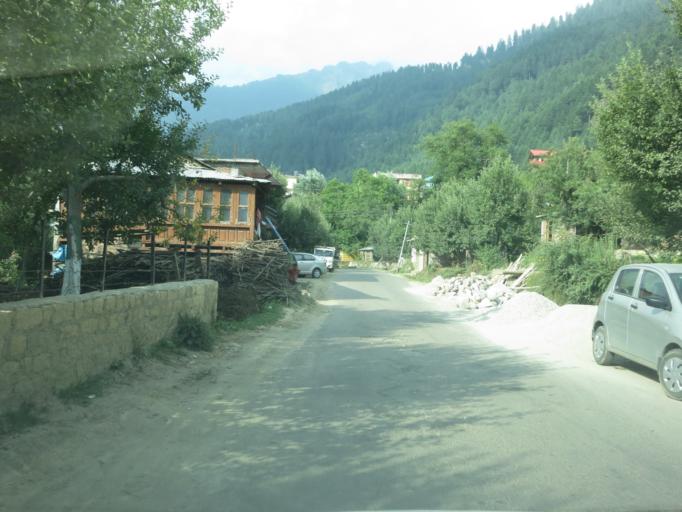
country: IN
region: Himachal Pradesh
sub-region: Kulu
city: Nagar
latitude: 32.1787
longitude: 77.1935
